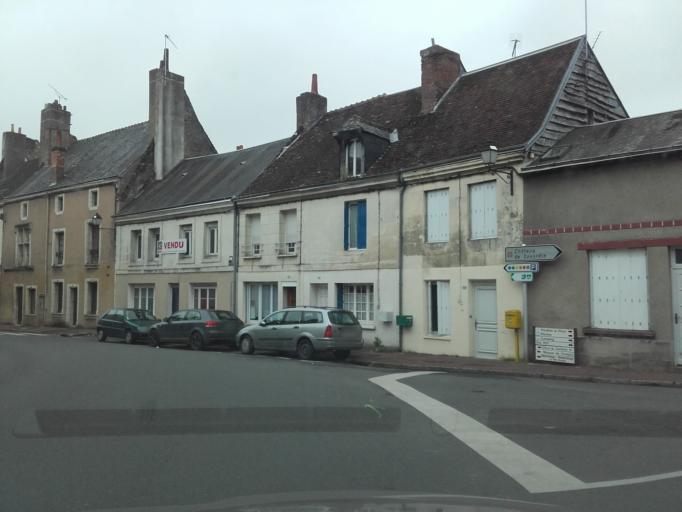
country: FR
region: Centre
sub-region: Departement du Loir-et-Cher
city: Montoire-sur-le-Loir
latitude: 47.7507
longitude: 0.8579
